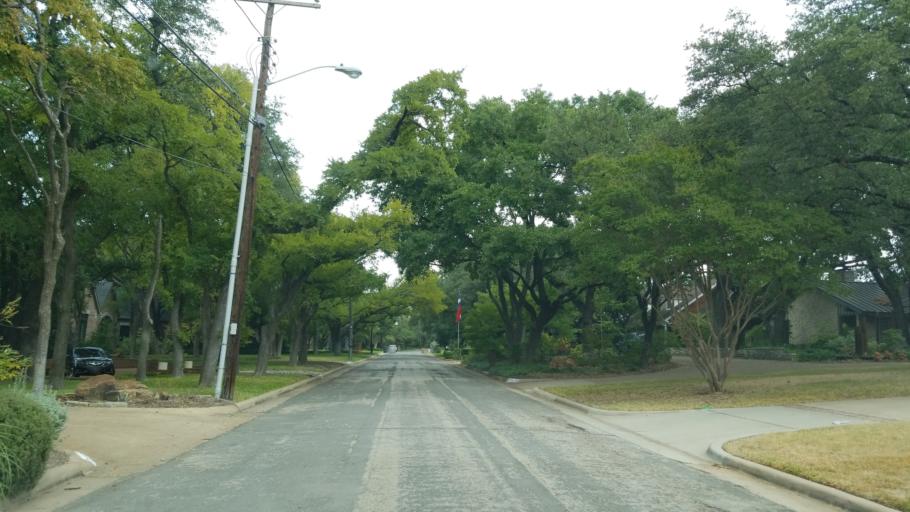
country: US
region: Texas
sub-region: Dallas County
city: Addison
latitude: 32.9356
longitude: -96.7840
